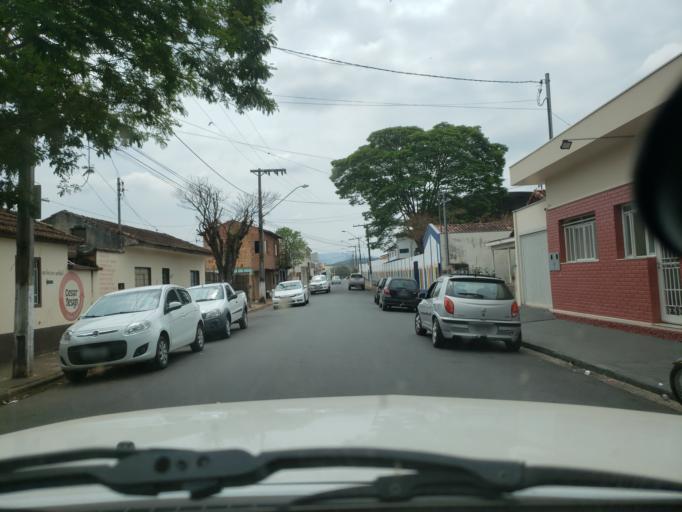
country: BR
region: Minas Gerais
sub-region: Jacutinga
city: Jacutinga
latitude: -22.2813
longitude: -46.6083
